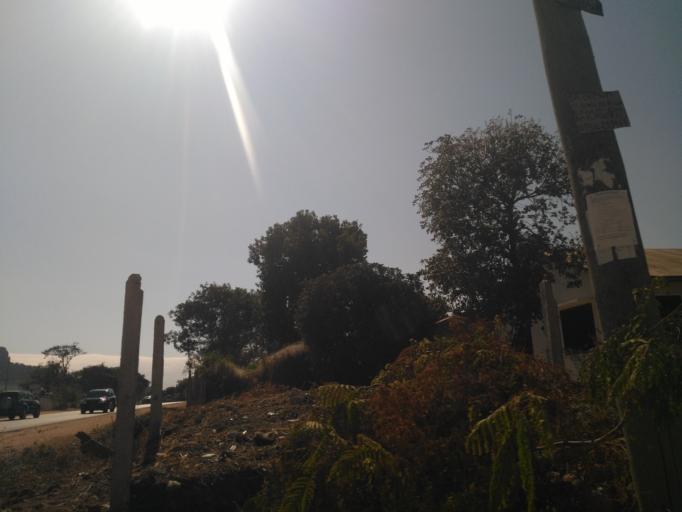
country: TZ
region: Dodoma
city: Dodoma
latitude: -6.1597
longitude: 35.7476
